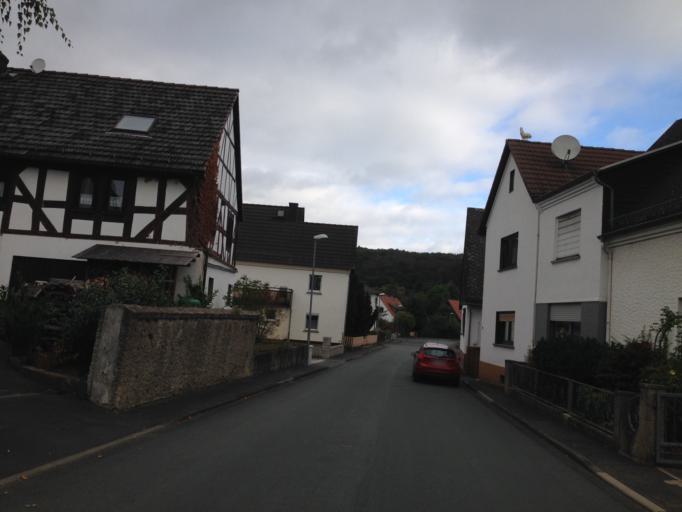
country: DE
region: Hesse
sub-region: Regierungsbezirk Giessen
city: Lohra
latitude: 50.6737
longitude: 8.5744
